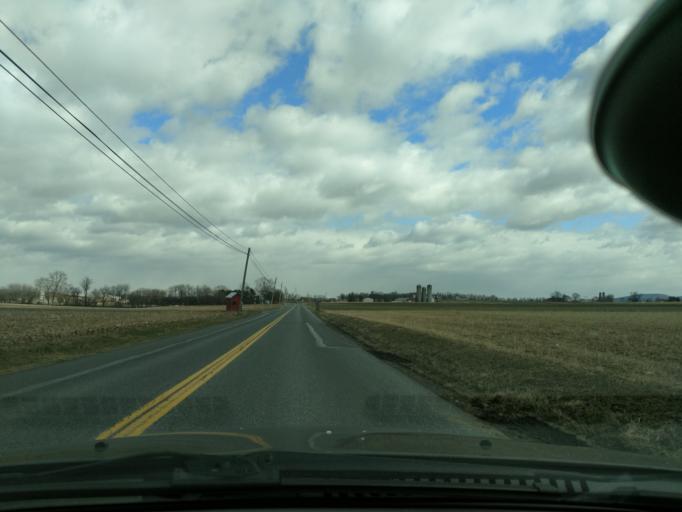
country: US
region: Pennsylvania
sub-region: Lebanon County
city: Myerstown
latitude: 40.3542
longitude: -76.3442
